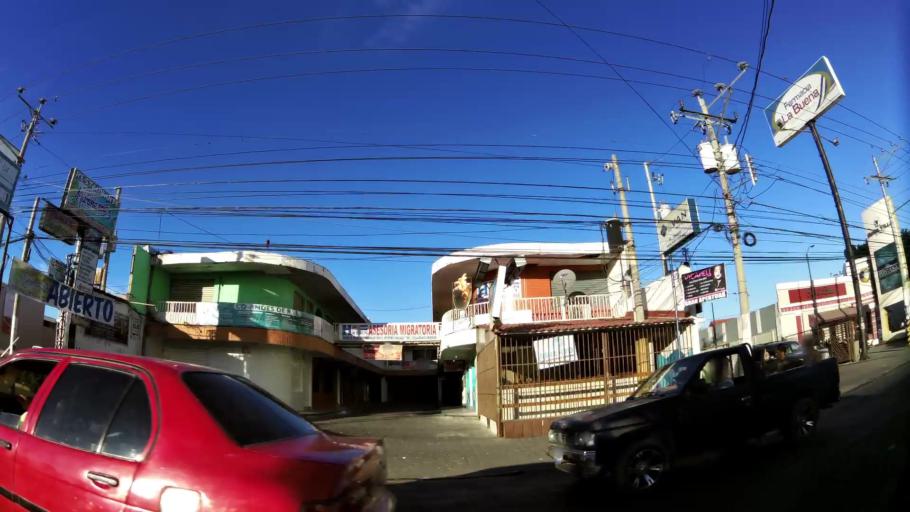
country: SV
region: San Miguel
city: San Miguel
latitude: 13.4842
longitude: -88.1854
